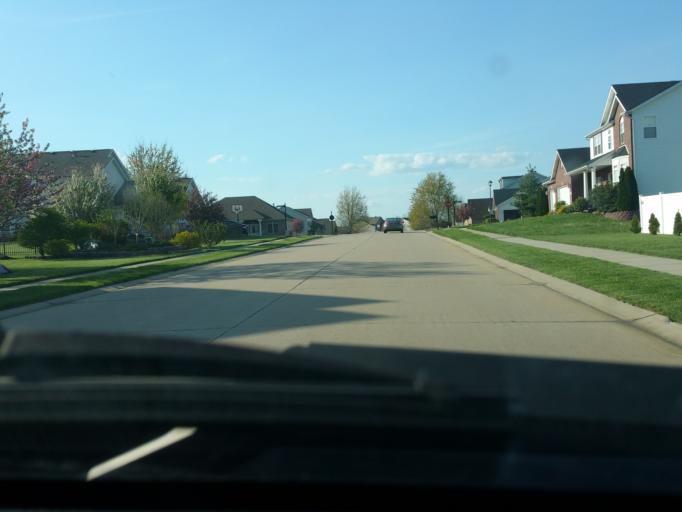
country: US
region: Illinois
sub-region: Madison County
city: Edwardsville
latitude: 38.7829
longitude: -89.9301
